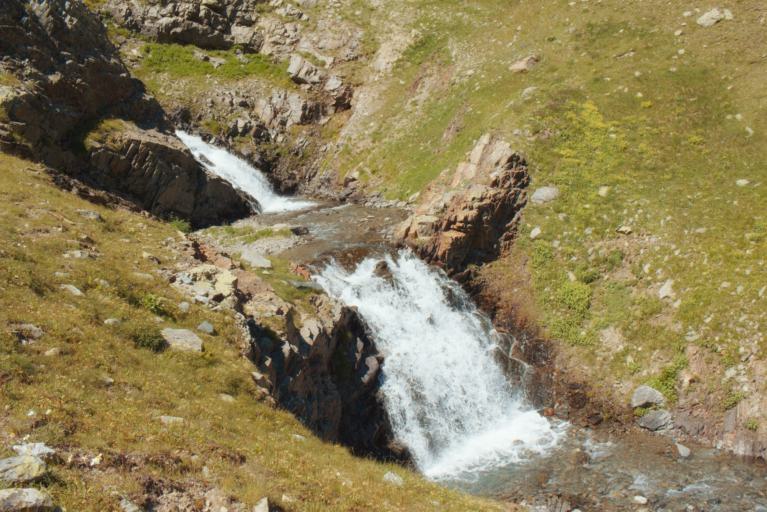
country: RU
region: Karachayevo-Cherkesiya
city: Mednogorskiy
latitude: 43.6292
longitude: 41.1231
